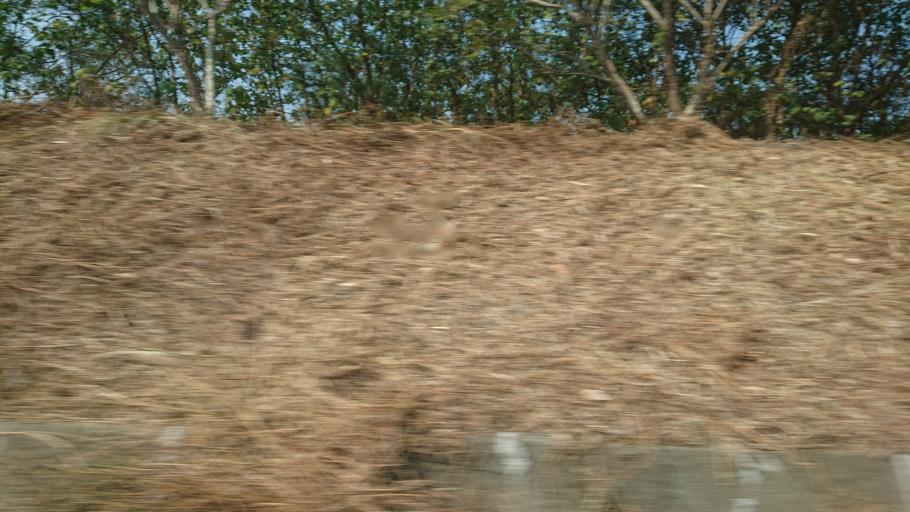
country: TW
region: Taiwan
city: Lugu
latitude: 23.7453
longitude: 120.6584
